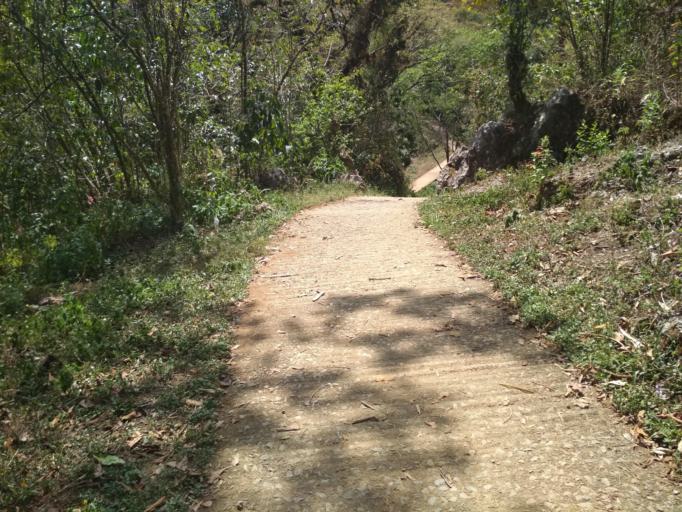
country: MX
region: Veracruz
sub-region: Tlilapan
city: Tonalixco
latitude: 18.7831
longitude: -97.0806
